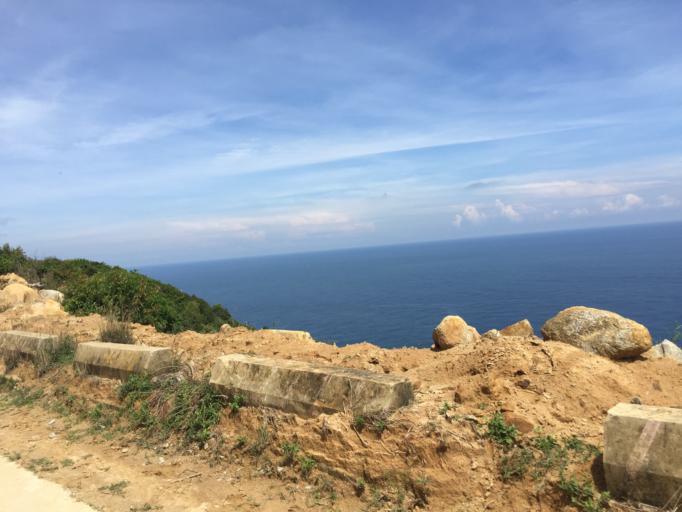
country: VN
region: Quang Nam
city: Hoi An
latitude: 15.9757
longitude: 108.5046
